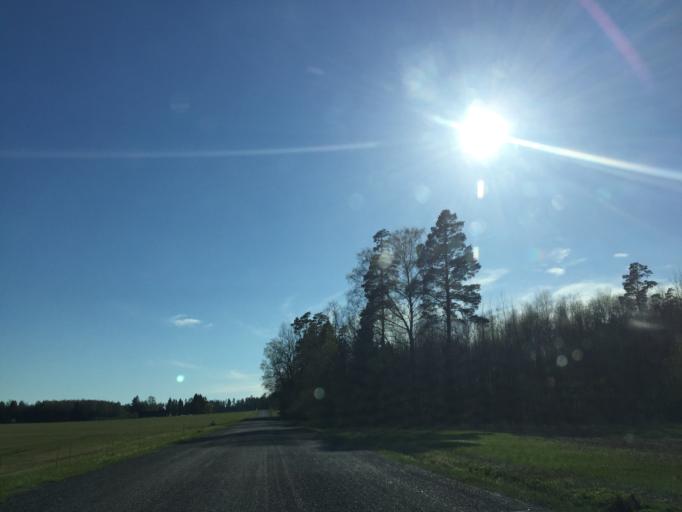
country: EE
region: Valgamaa
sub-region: Valga linn
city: Valga
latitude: 57.8289
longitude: 26.2203
